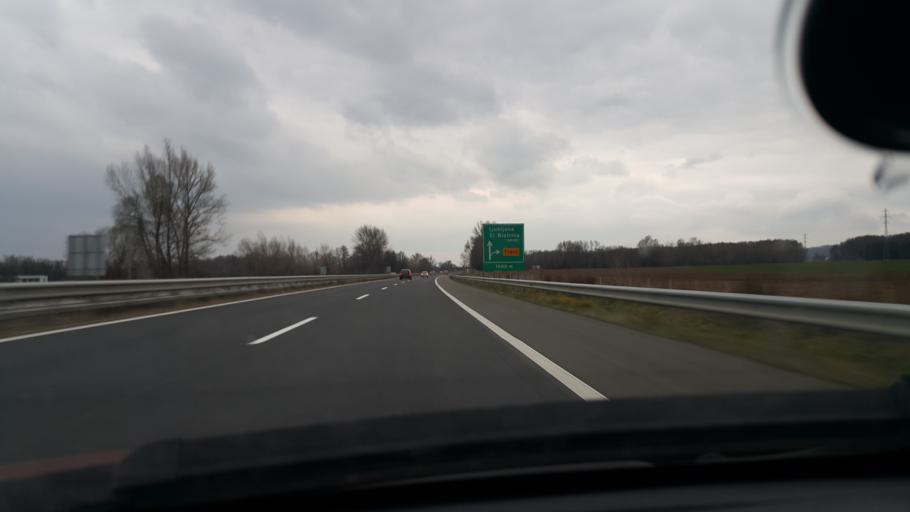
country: SI
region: Hoce-Slivnica
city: Hotinja Vas
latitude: 46.4607
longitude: 15.6563
